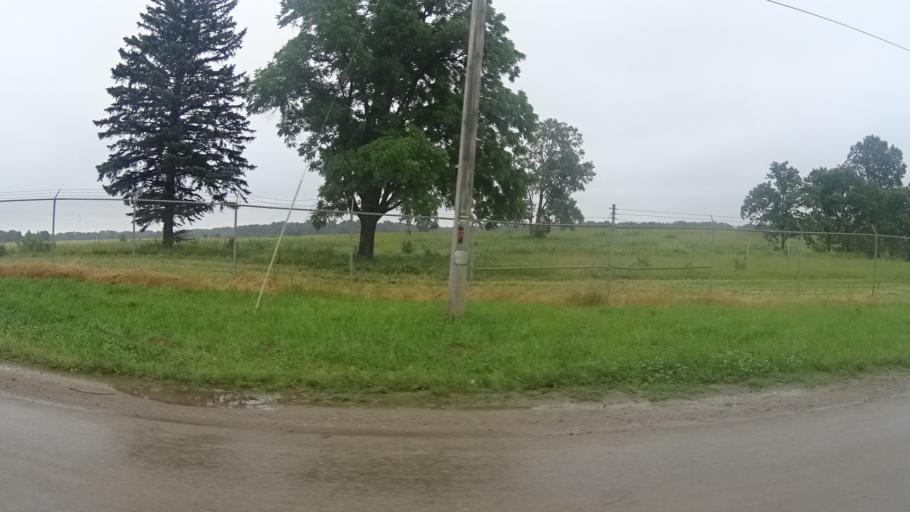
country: US
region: Ohio
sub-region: Erie County
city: Milan
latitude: 41.3468
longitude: -82.6056
